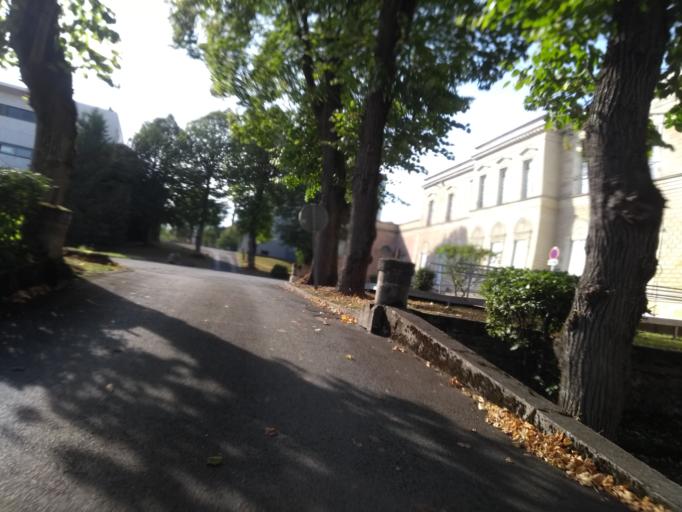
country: FR
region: Aquitaine
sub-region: Departement de la Gironde
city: Talence
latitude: 44.8101
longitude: -0.5927
